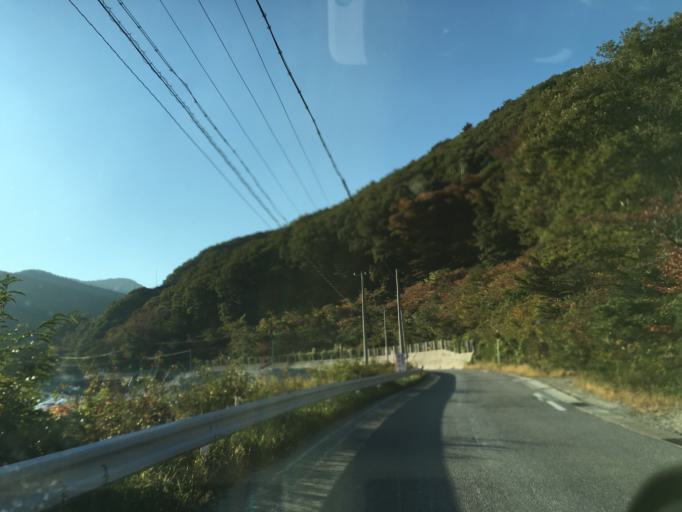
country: JP
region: Fukushima
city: Koriyama
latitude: 37.3912
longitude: 140.2151
